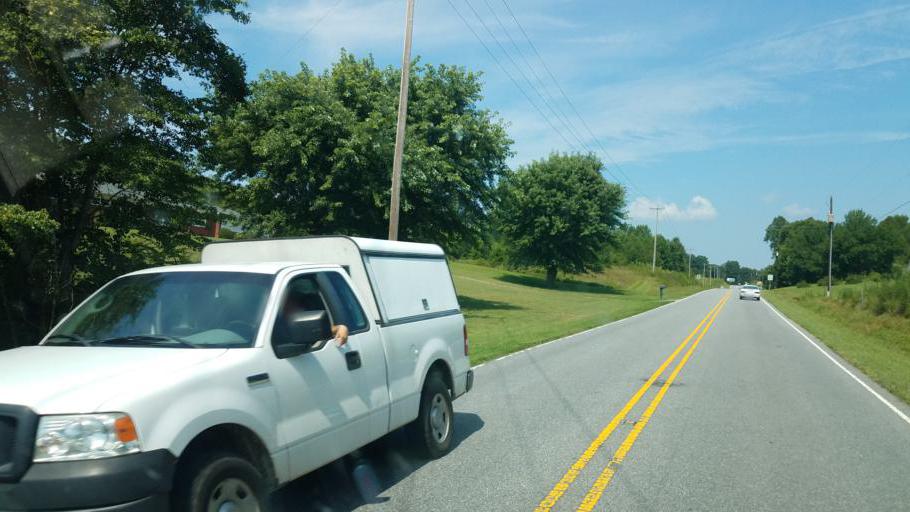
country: US
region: North Carolina
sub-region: Burke County
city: Icard
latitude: 35.5564
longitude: -81.5072
